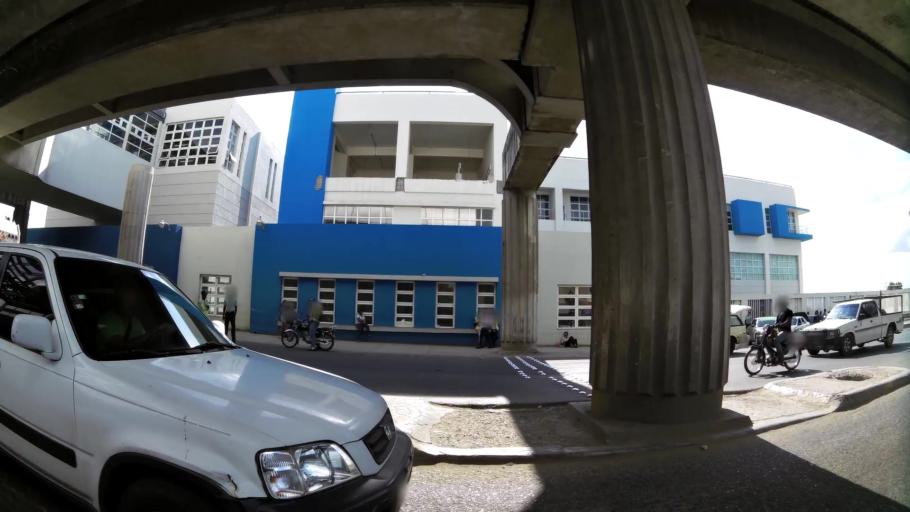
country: DO
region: Nacional
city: Ensanche Luperon
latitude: 18.5469
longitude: -69.9010
